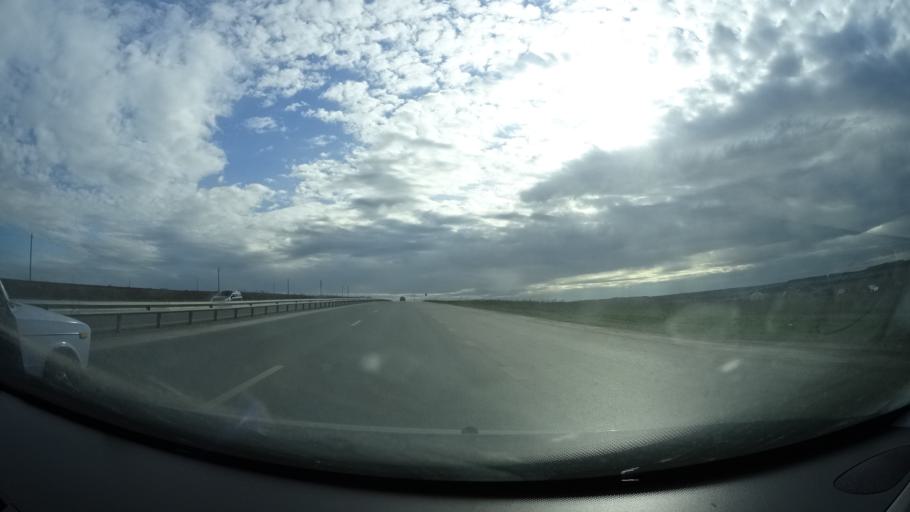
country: RU
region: Perm
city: Kultayevo
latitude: 57.8713
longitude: 55.8942
